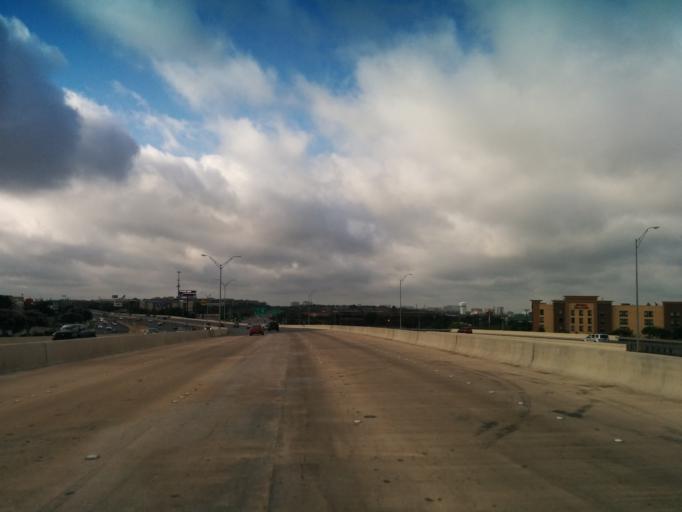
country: US
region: Texas
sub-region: Bexar County
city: Shavano Park
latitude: 29.5504
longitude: -98.5854
